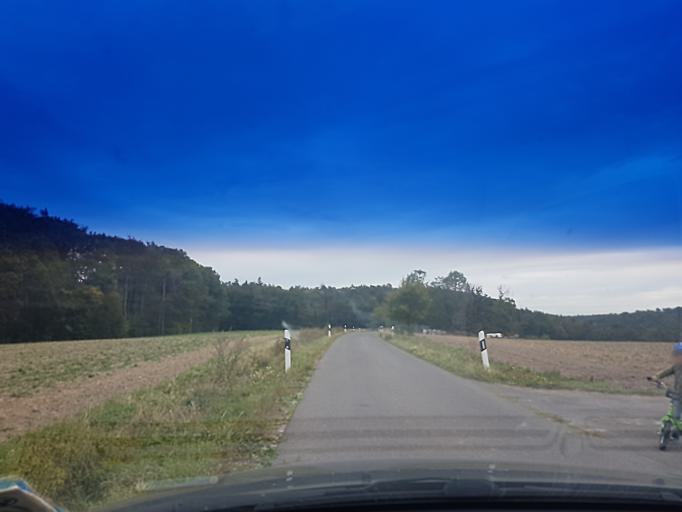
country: DE
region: Bavaria
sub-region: Regierungsbezirk Unterfranken
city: Geiselwind
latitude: 49.8229
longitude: 10.4914
